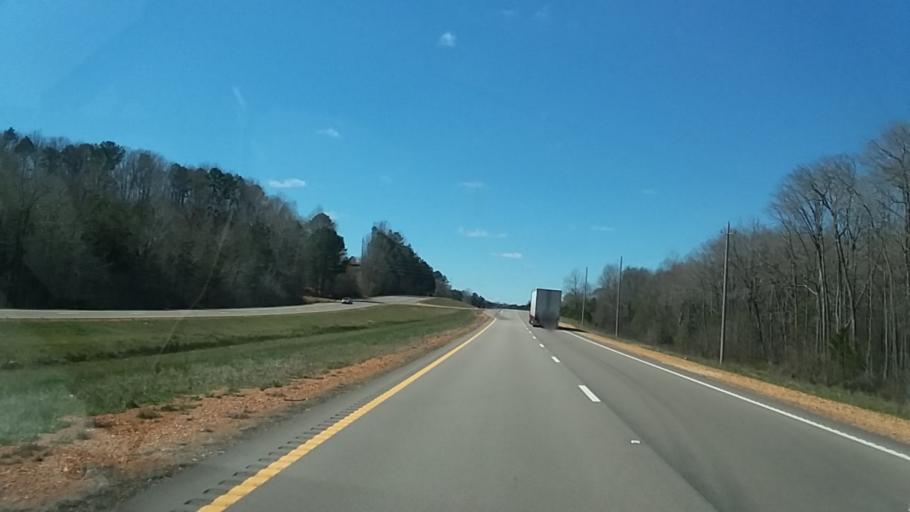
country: US
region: Mississippi
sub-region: Alcorn County
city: Farmington
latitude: 34.8580
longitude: -88.3926
